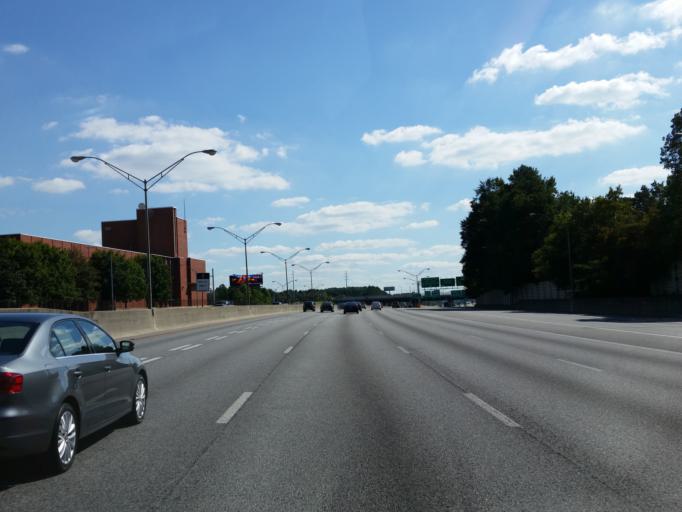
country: US
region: Georgia
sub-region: Fulton County
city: Hapeville
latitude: 33.6575
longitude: -84.3950
